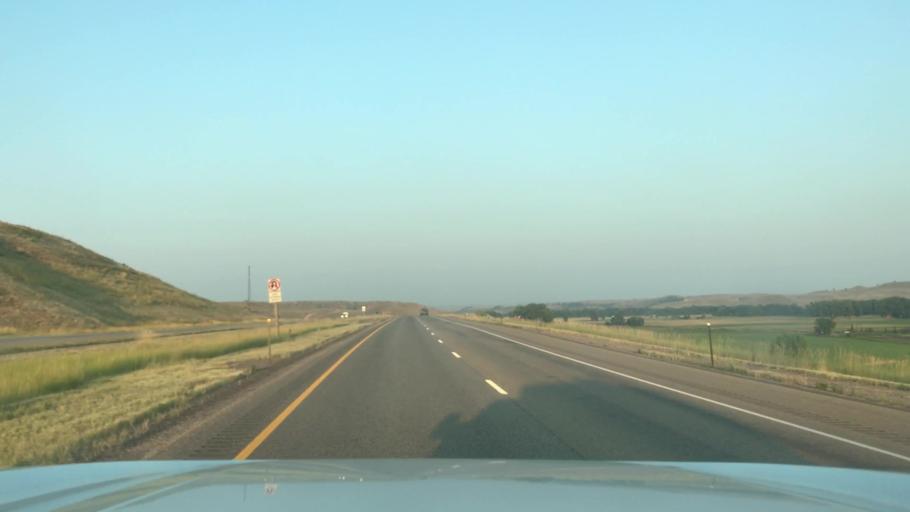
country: US
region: Wyoming
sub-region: Sheridan County
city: Sheridan
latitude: 44.9145
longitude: -107.0786
